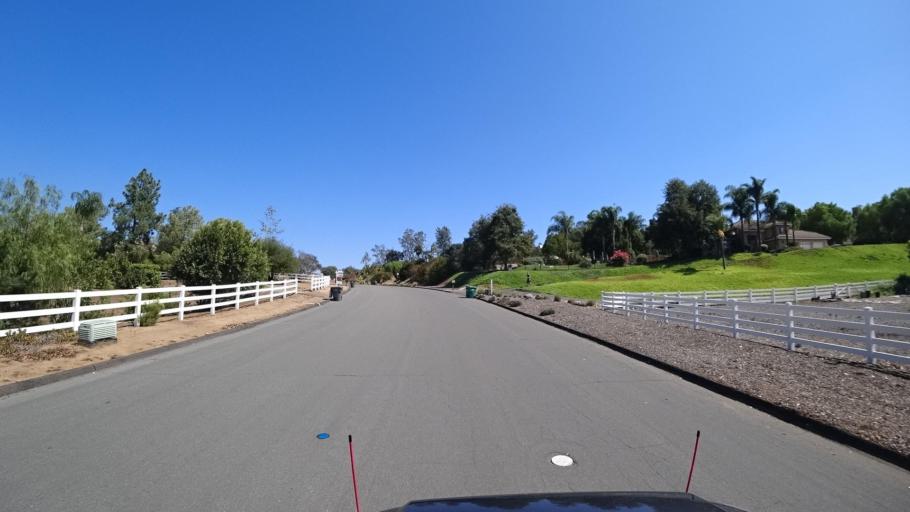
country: US
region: California
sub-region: San Diego County
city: Harbison Canyon
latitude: 32.8247
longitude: -116.8520
